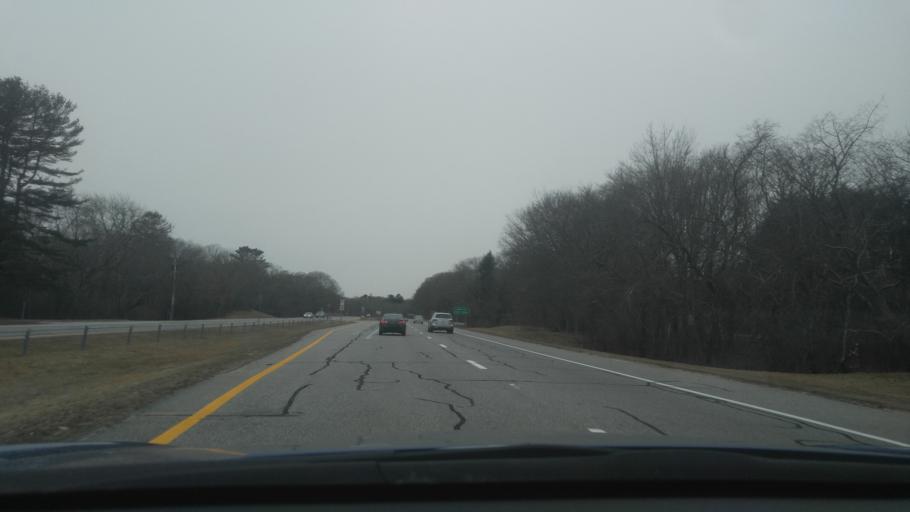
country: US
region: Rhode Island
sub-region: Washington County
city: Wakefield-Peacedale
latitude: 41.4273
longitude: -71.5130
